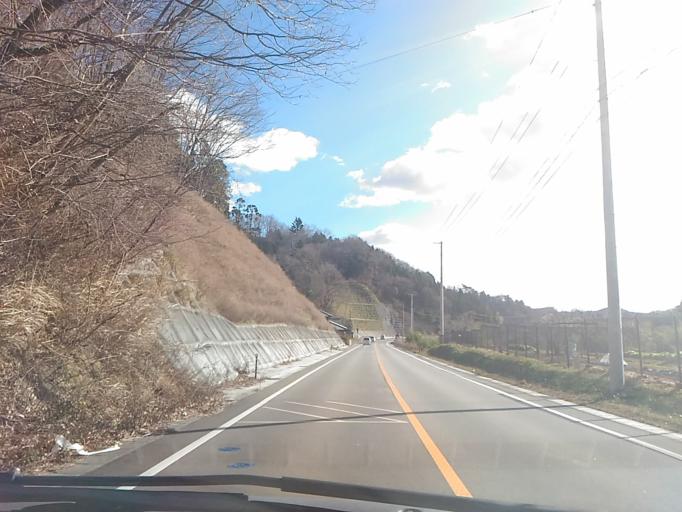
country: JP
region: Fukushima
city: Iwaki
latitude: 37.0144
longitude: 140.7707
